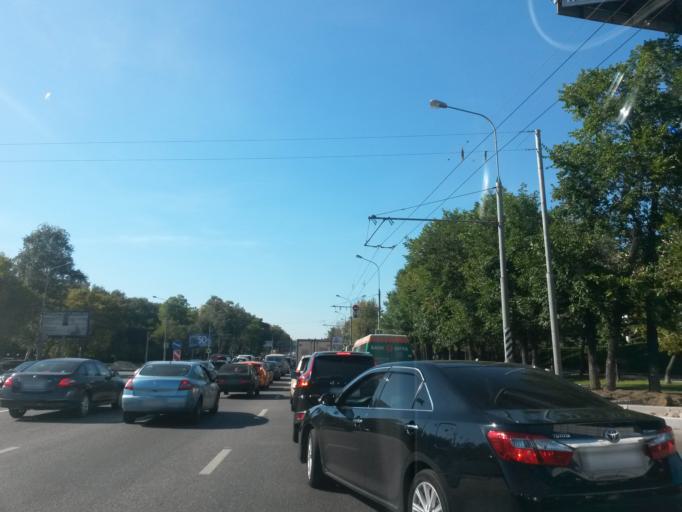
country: RU
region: Moscow
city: Tsaritsyno
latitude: 55.6560
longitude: 37.6471
